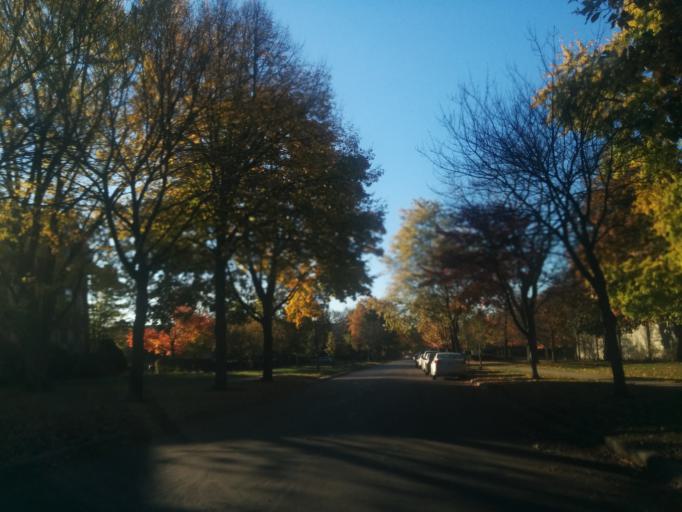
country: US
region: Illinois
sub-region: Cook County
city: River Forest
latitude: 41.9006
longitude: -87.8071
